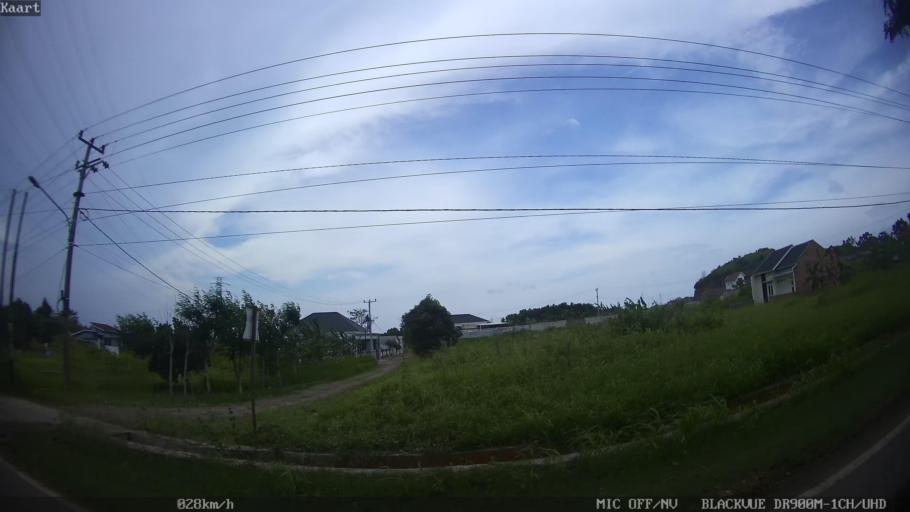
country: ID
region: Lampung
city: Bandarlampung
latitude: -5.4076
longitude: 105.1946
